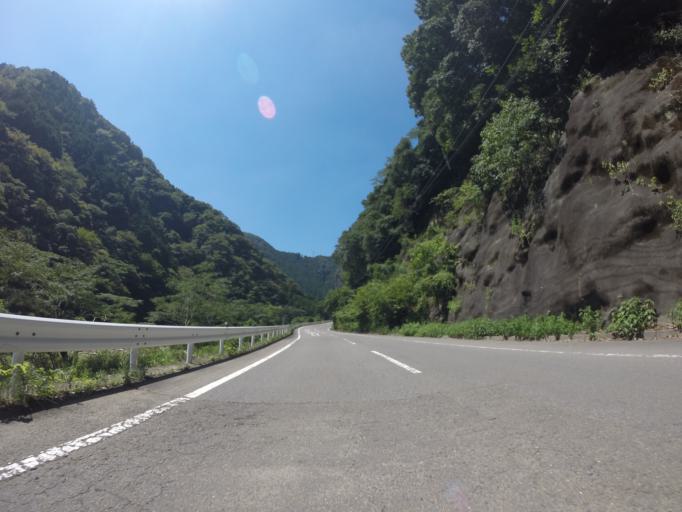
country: JP
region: Shizuoka
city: Shizuoka-shi
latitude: 35.0410
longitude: 138.2559
